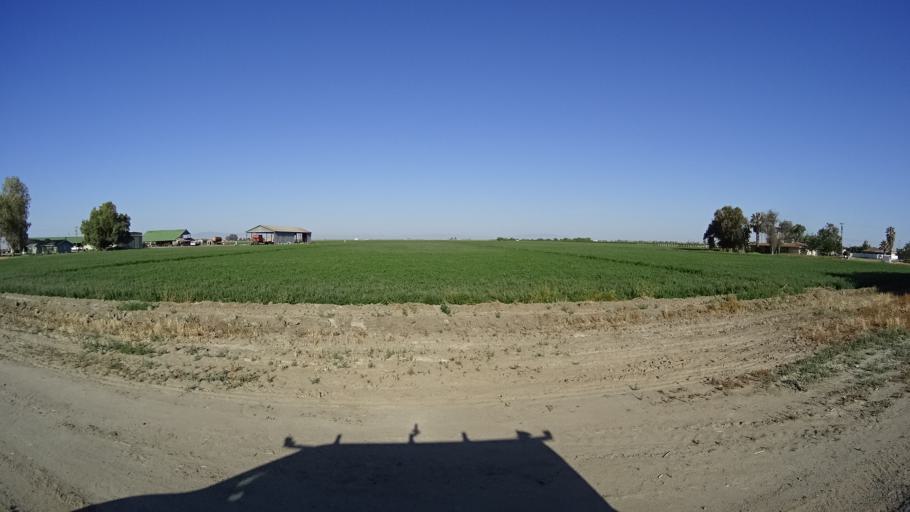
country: US
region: California
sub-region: Kings County
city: Stratford
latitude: 36.1729
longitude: -119.7982
